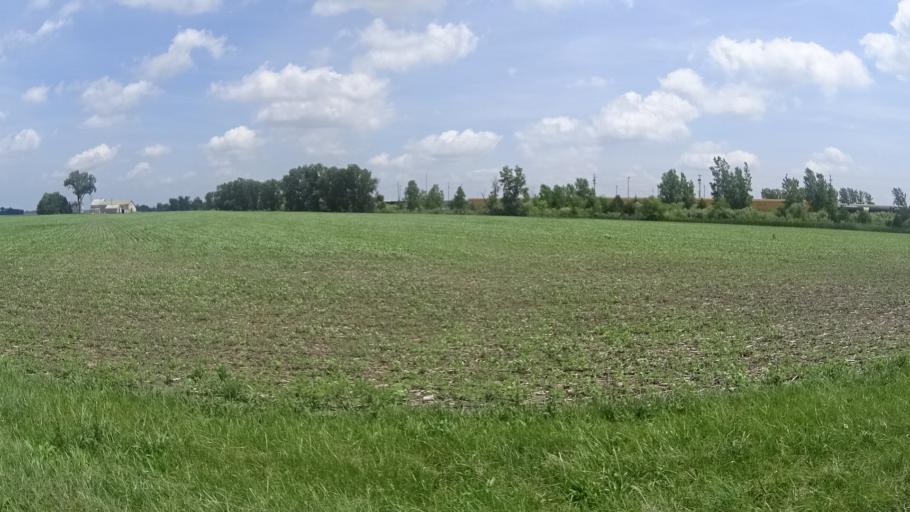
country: US
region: Ohio
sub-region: Huron County
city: Bellevue
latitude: 41.2991
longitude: -82.7681
